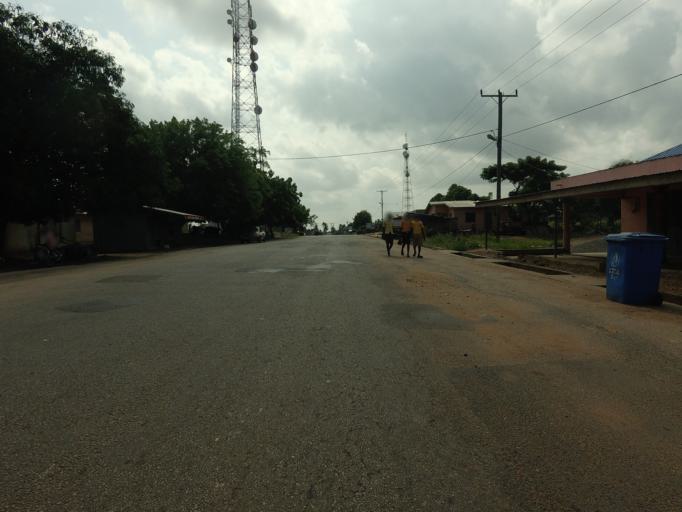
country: GH
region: Volta
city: Ho
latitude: 6.4165
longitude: 0.7450
